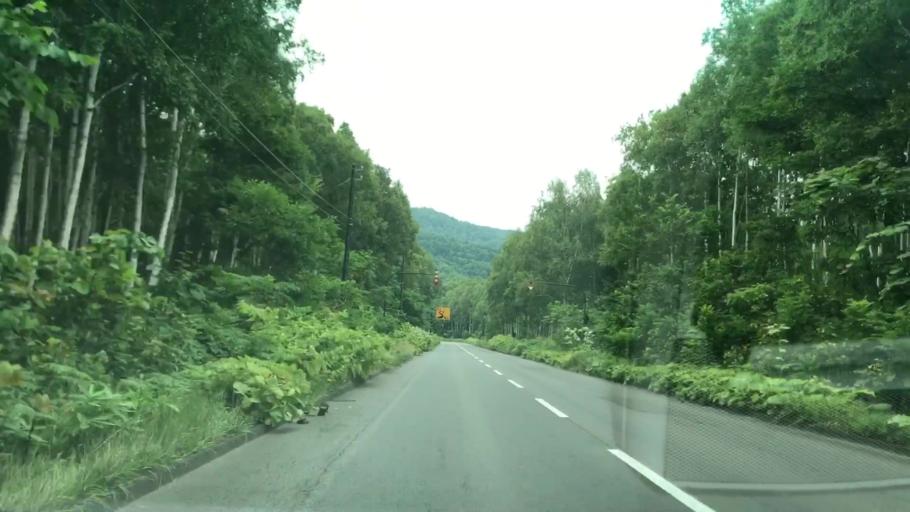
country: JP
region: Hokkaido
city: Yoichi
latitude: 43.0085
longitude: 140.8735
